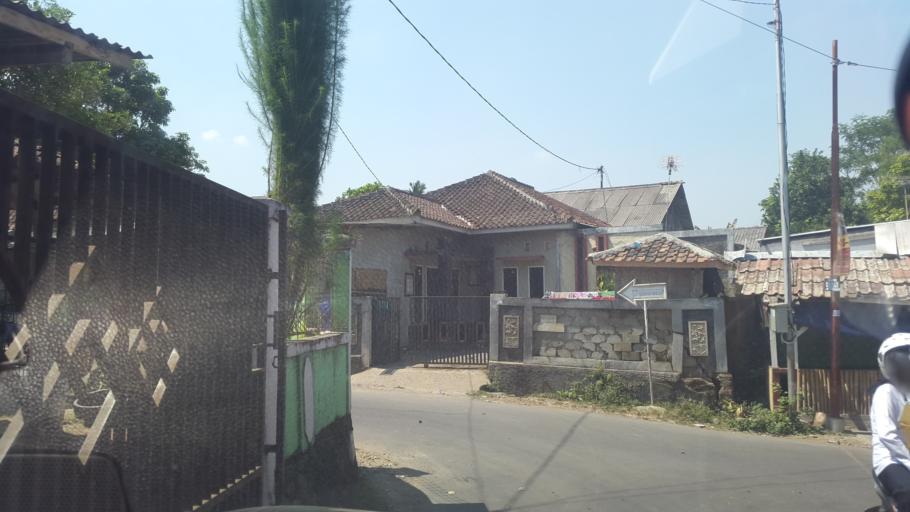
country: ID
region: West Java
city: Cicurug
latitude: -6.8848
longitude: 106.8201
